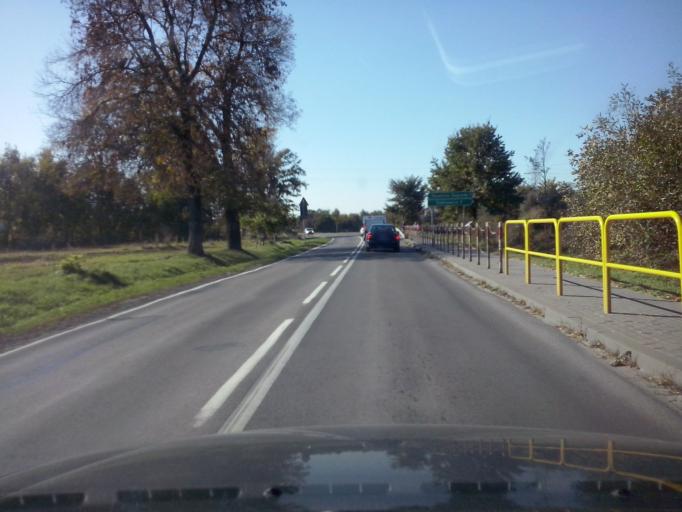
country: PL
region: Lublin Voivodeship
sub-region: Powiat bilgorajski
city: Bilgoraj
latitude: 50.5205
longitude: 22.6820
